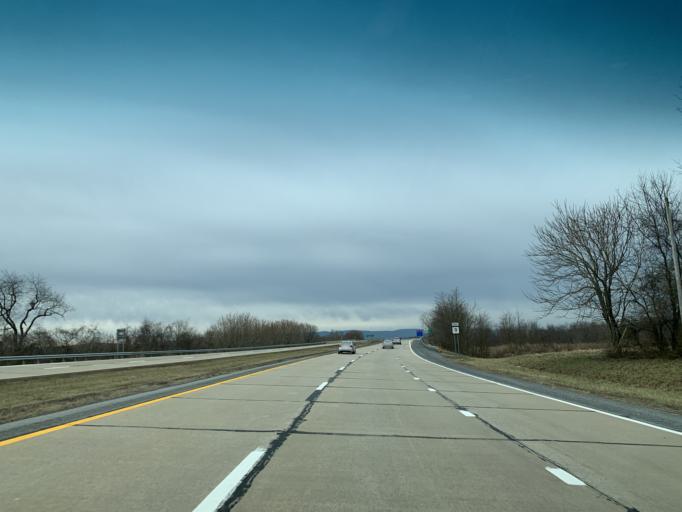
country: US
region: West Virginia
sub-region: Jefferson County
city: Ranson
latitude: 39.3287
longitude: -77.8548
